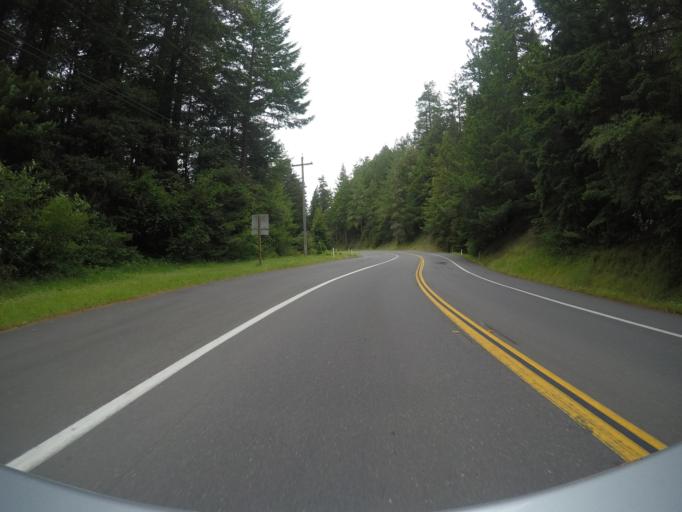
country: US
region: California
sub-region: Humboldt County
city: Rio Dell
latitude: 40.4029
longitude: -123.9509
